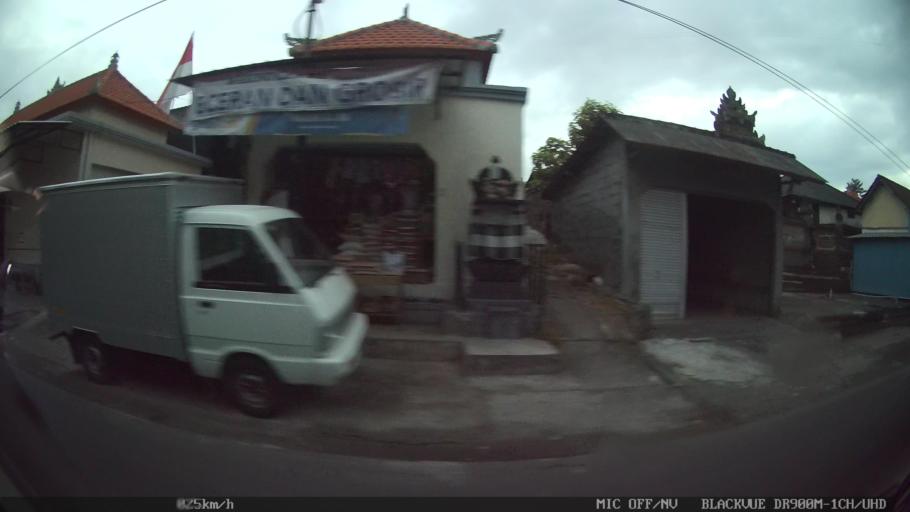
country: ID
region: Bali
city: Banjar Kertajiwa
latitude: -8.6340
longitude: 115.2610
